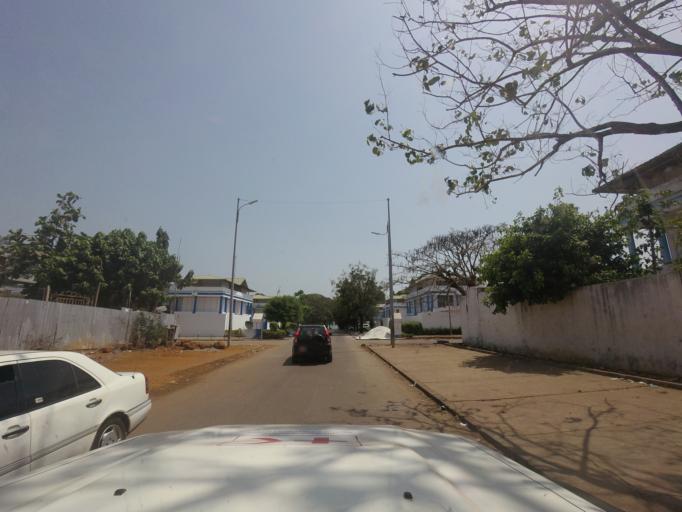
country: GN
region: Conakry
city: Camayenne
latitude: 9.5078
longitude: -13.7166
